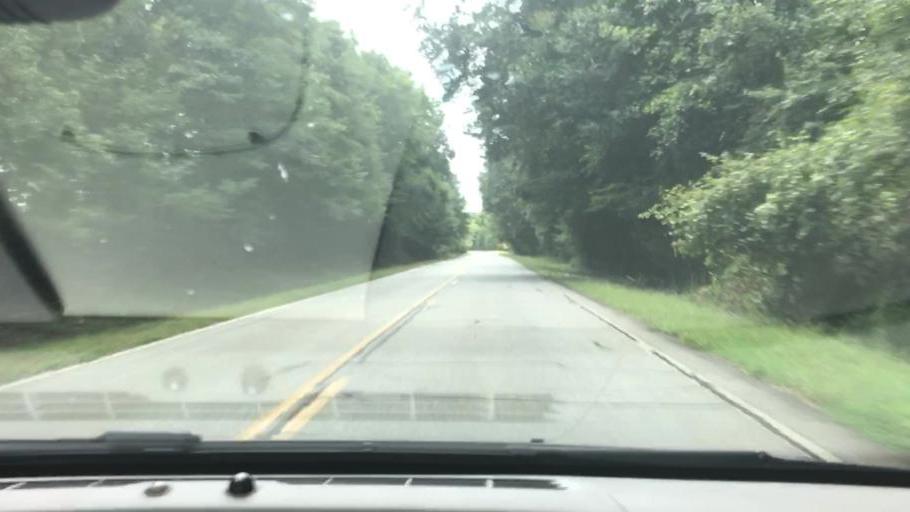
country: US
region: Georgia
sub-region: Quitman County
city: Georgetown
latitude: 32.0947
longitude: -85.0399
